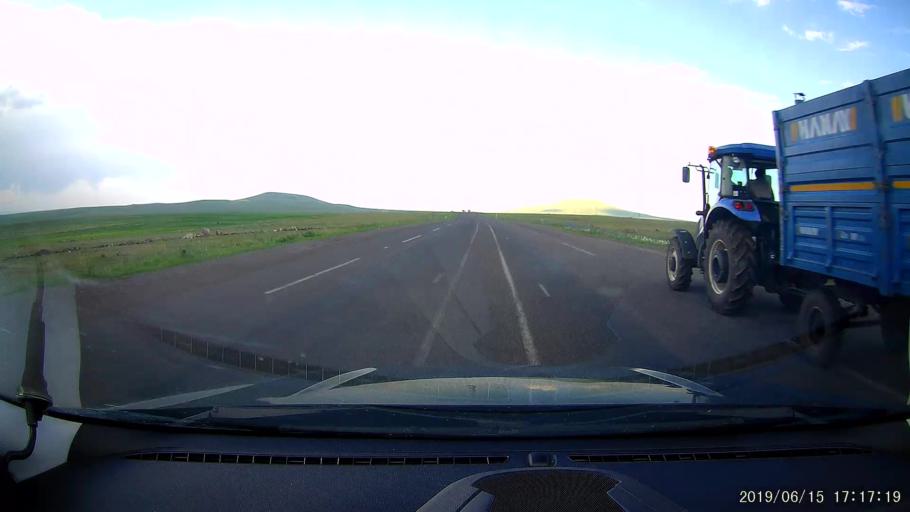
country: TR
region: Kars
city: Kars
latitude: 40.6145
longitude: 43.2362
